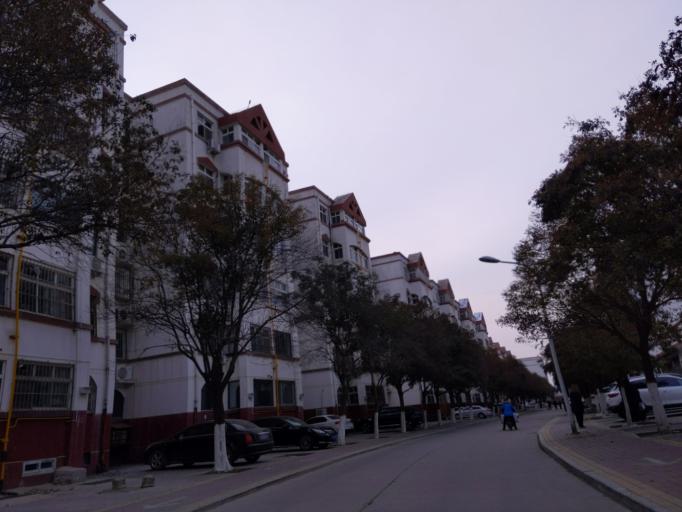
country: CN
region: Henan Sheng
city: Zhongyuanlu
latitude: 35.7563
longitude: 115.0529
